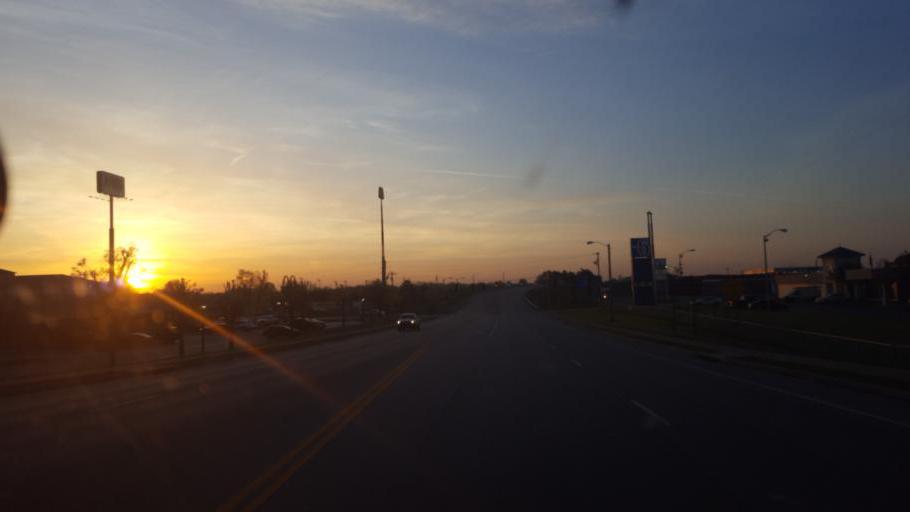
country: US
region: Kentucky
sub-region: Barren County
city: Cave City
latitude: 37.1344
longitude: -85.9739
